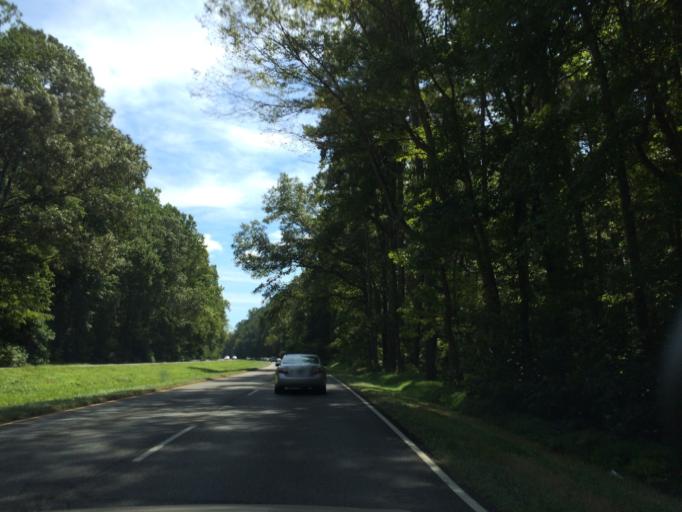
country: US
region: Virginia
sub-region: York County
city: Yorktown
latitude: 37.2098
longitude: -76.5121
